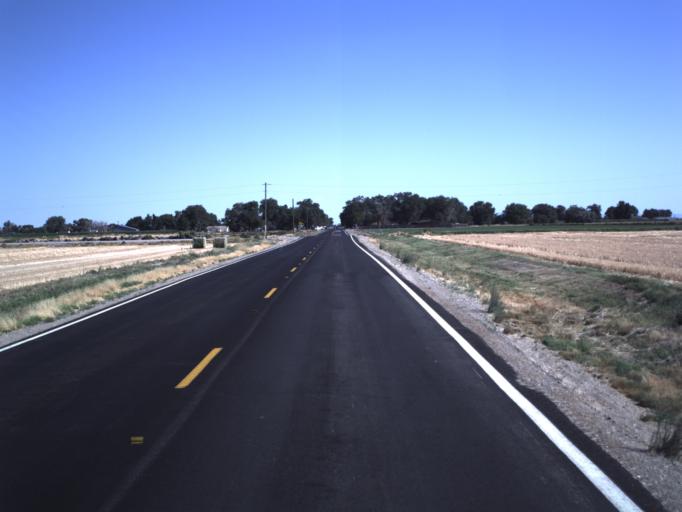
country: US
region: Utah
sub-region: Millard County
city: Delta
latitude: 39.2784
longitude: -112.6529
